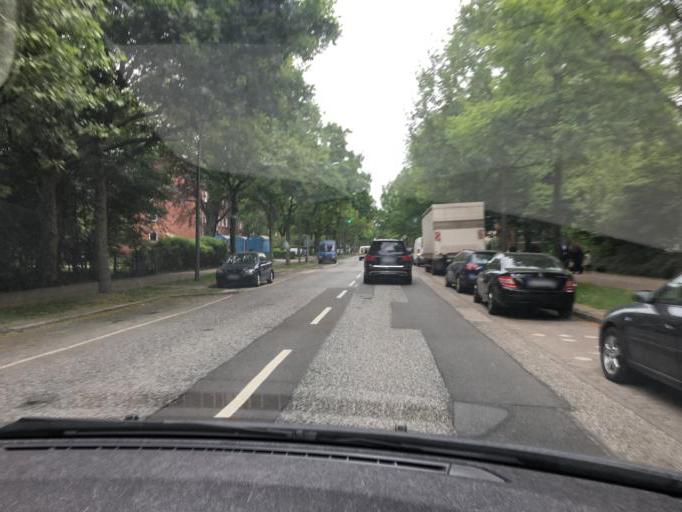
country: DE
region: Hamburg
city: Kleiner Grasbrook
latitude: 53.5111
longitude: 9.9928
